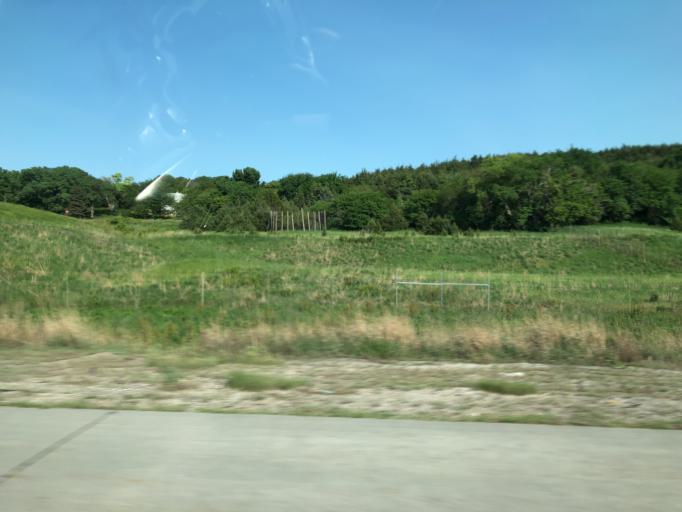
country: US
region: Nebraska
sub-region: Sarpy County
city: Gretna
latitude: 41.0710
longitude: -96.2859
